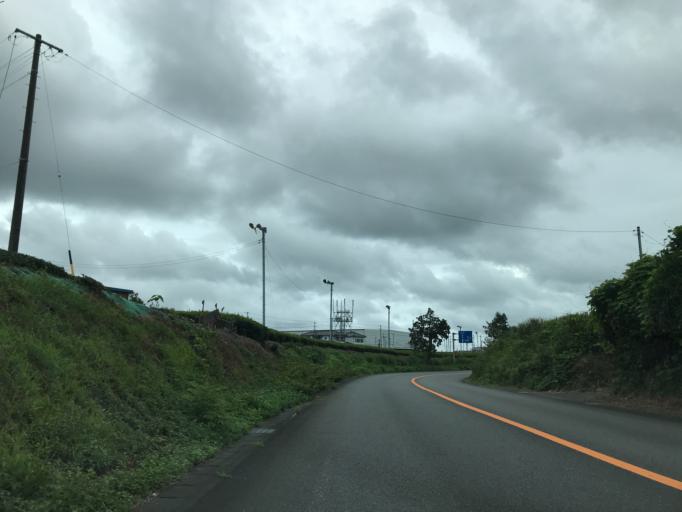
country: JP
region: Shizuoka
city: Kanaya
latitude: 34.7730
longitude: 138.1405
